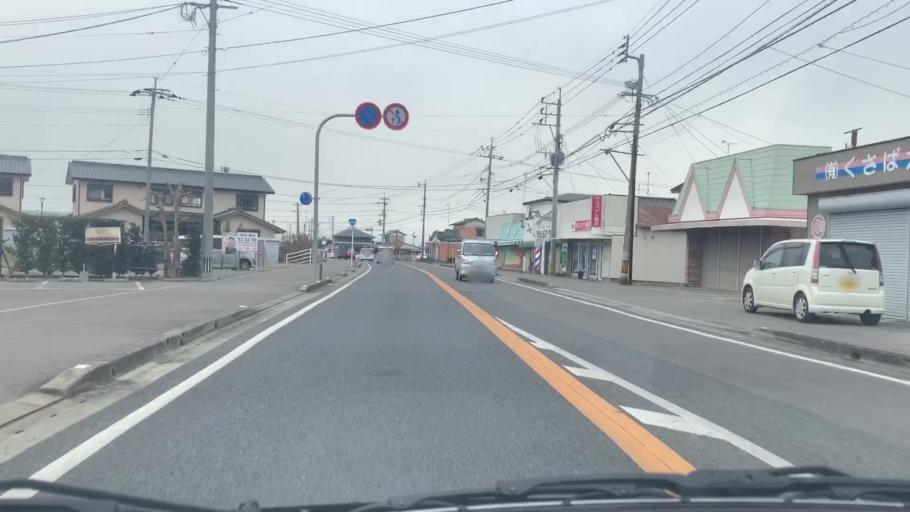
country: JP
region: Saga Prefecture
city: Saga-shi
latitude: 33.1842
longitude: 130.1915
